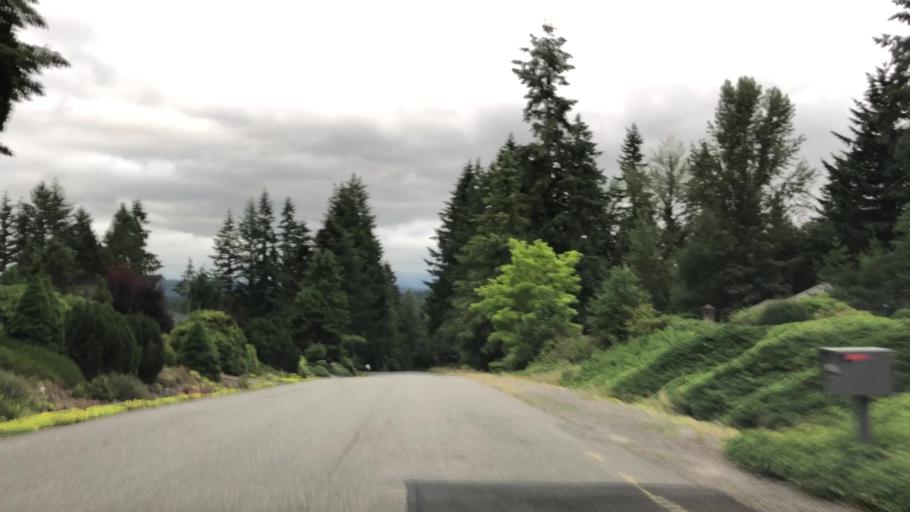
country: US
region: Washington
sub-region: King County
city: Cottage Lake
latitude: 47.7198
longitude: -122.0941
